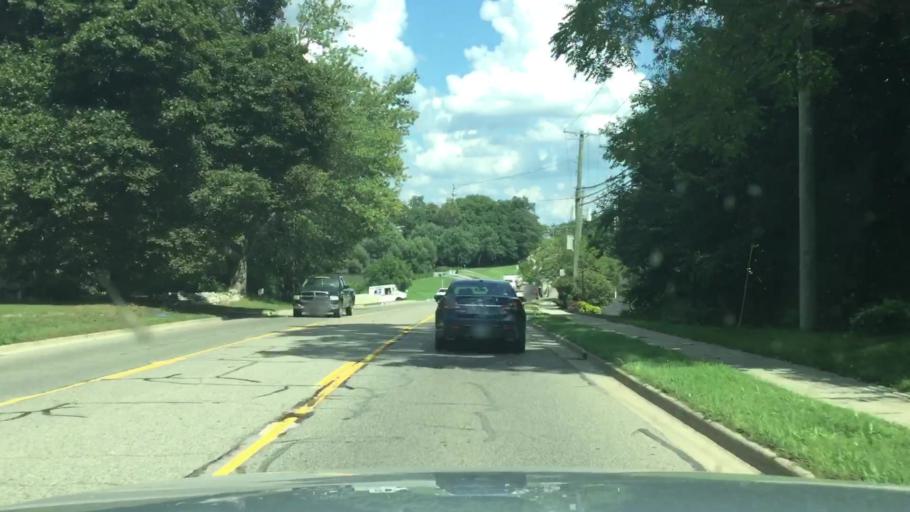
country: US
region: Michigan
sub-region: Washtenaw County
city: Saline
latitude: 42.1624
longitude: -83.7921
